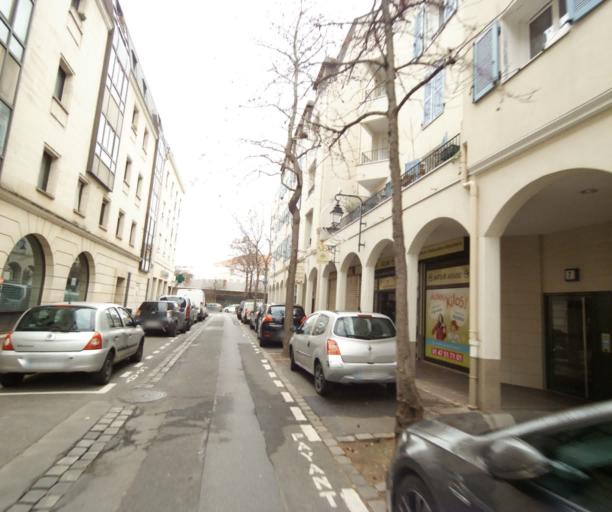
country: FR
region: Ile-de-France
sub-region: Departement des Hauts-de-Seine
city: Rueil-Malmaison
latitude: 48.8800
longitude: 2.1845
